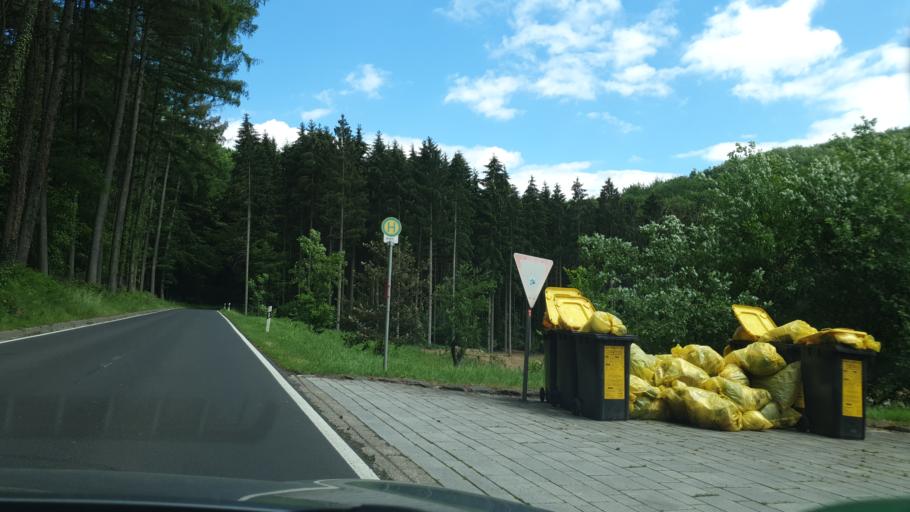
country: DE
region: Rheinland-Pfalz
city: Neuhausel
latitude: 50.3983
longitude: 7.7151
